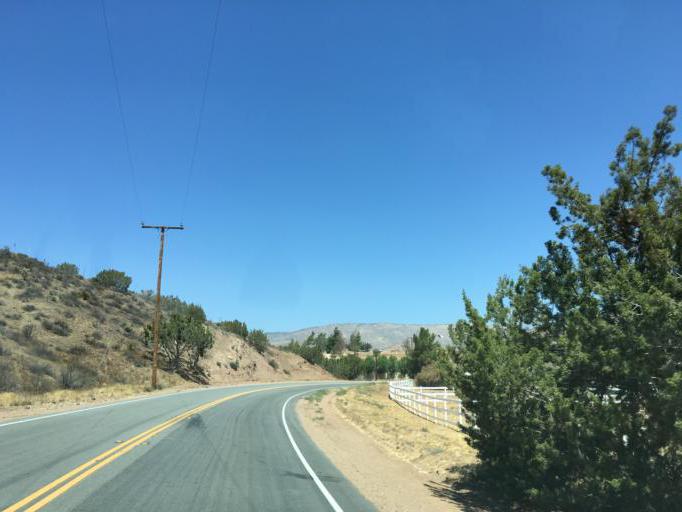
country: US
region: California
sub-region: Los Angeles County
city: Acton
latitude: 34.4836
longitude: -118.2139
